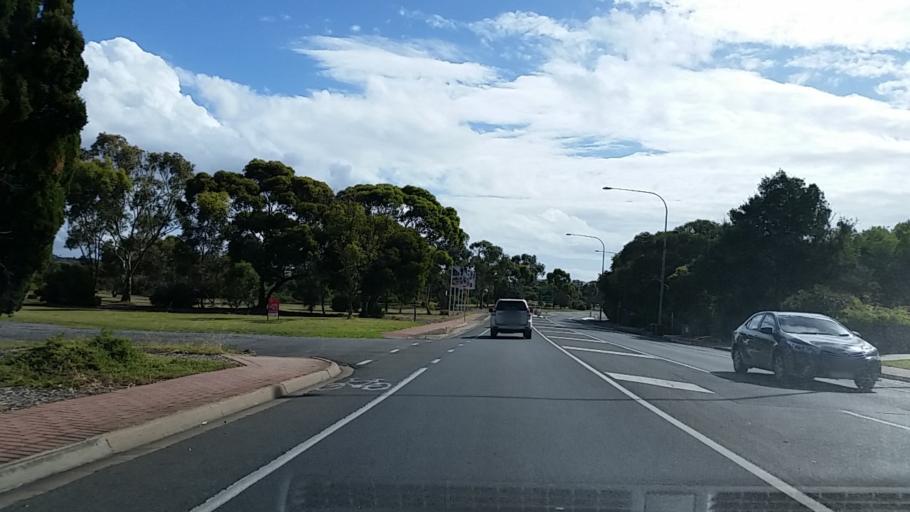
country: AU
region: South Australia
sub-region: Adelaide
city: Port Noarlunga
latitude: -35.1475
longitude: 138.4759
